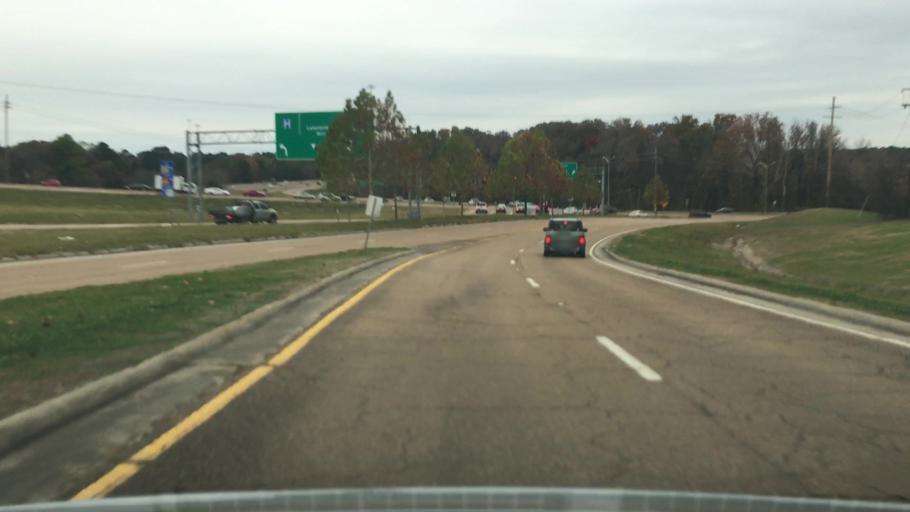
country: US
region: Mississippi
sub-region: Rankin County
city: Flowood
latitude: 32.3321
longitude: -90.1610
